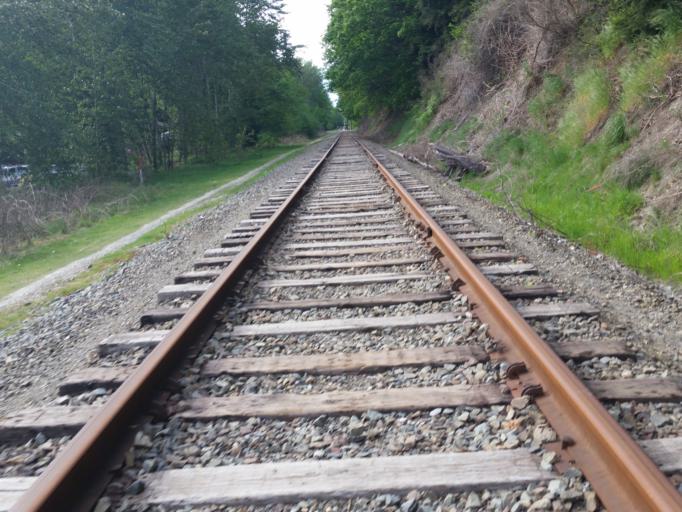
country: US
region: Washington
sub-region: King County
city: Yarrow Point
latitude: 47.6424
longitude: -122.1918
